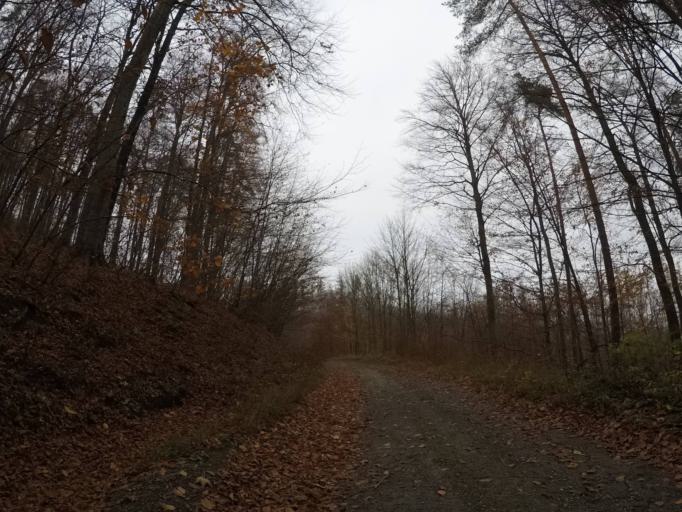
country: SK
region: Presovsky
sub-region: Okres Presov
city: Presov
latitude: 48.8949
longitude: 21.1978
